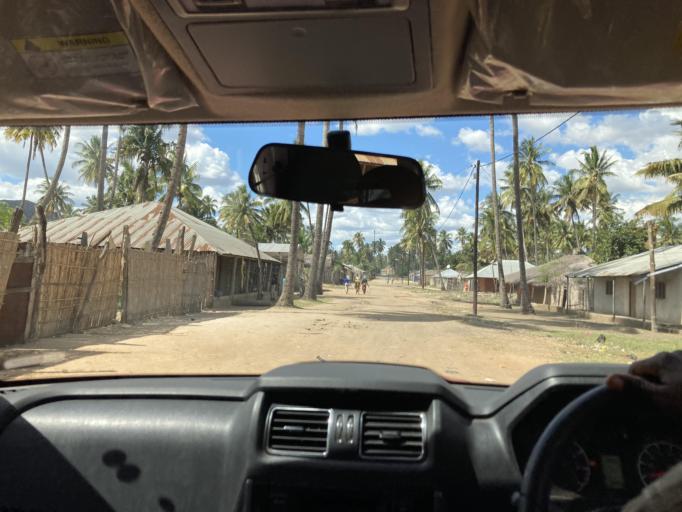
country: MZ
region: Cabo Delgado
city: Montepuez
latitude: -13.1308
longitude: 39.0059
